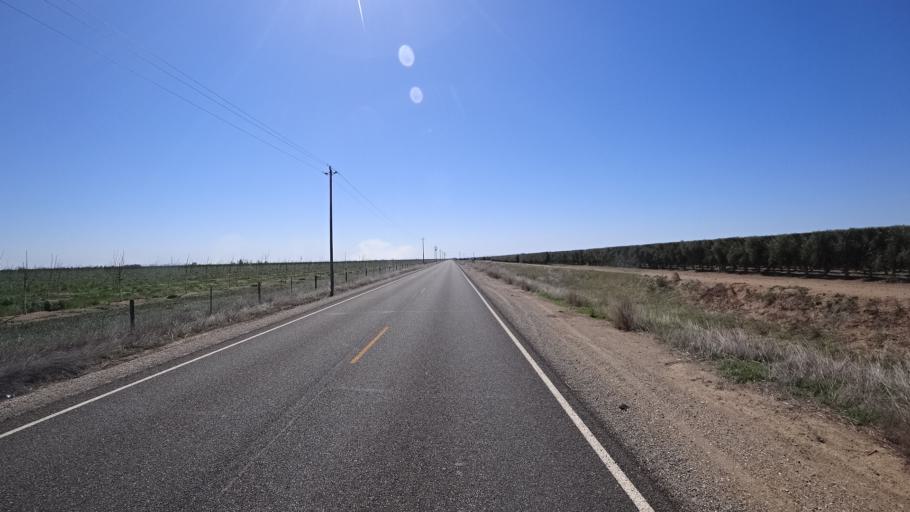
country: US
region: California
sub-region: Glenn County
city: Willows
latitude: 39.6017
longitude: -122.2498
